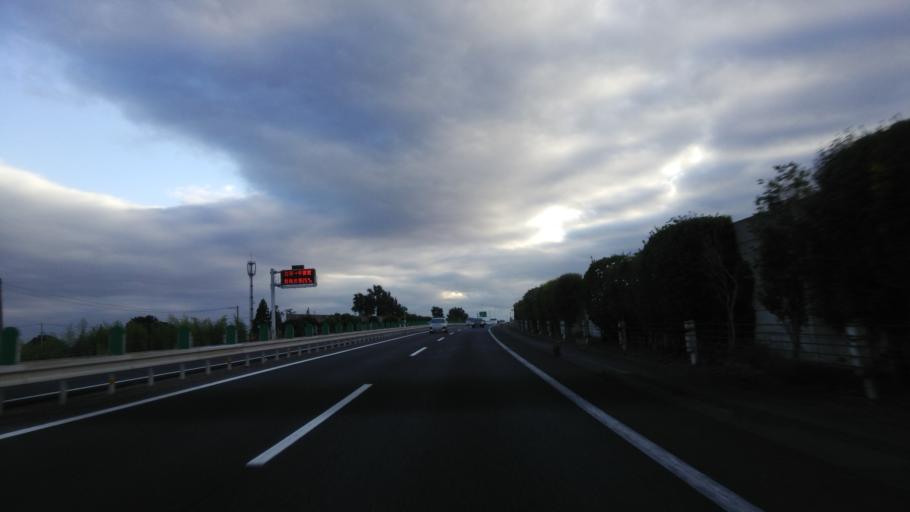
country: JP
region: Fukushima
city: Koriyama
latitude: 37.4396
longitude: 140.3492
